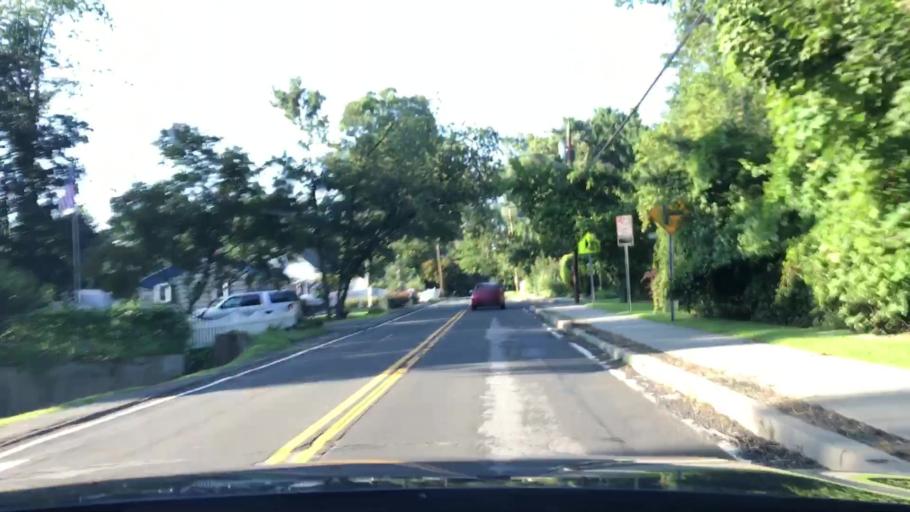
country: US
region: New Jersey
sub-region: Bergen County
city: Northvale
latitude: 41.0100
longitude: -73.9294
